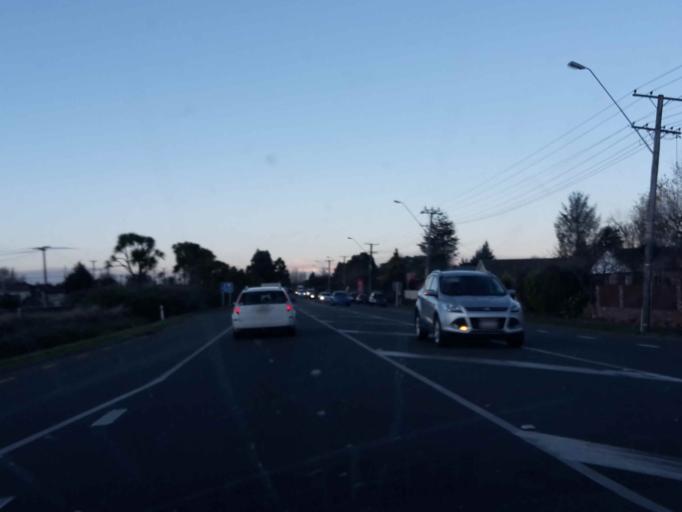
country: NZ
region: Canterbury
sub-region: Selwyn District
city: Prebbleton
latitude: -43.5544
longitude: 172.4745
